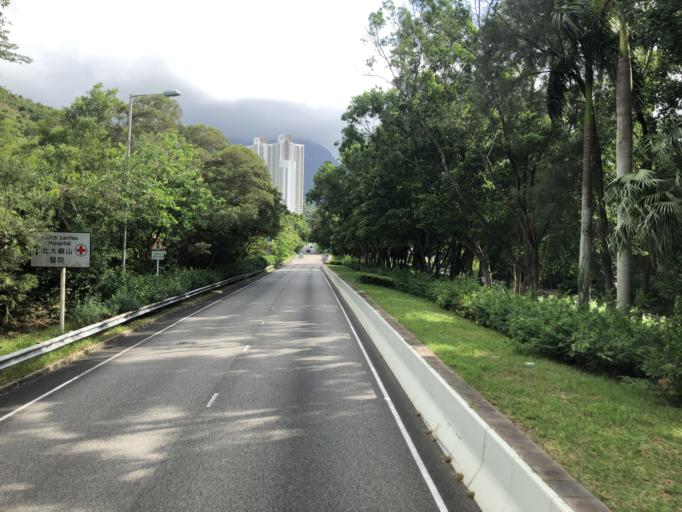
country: HK
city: Tai O
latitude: 22.2861
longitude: 113.9442
